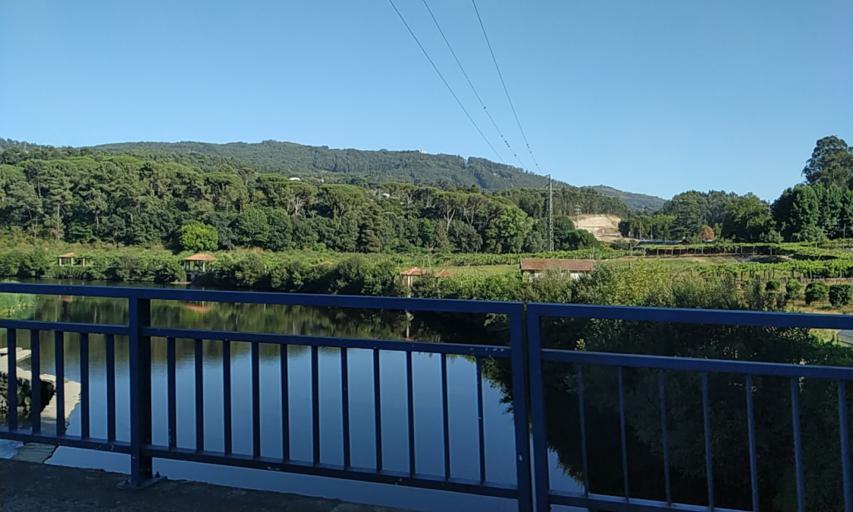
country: PT
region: Porto
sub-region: Santo Tirso
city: Santo Tirso
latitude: 41.3462
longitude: -8.4705
